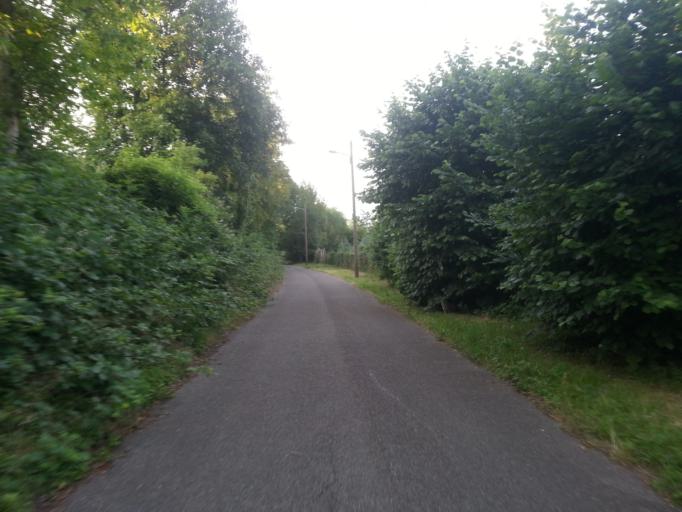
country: DE
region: Baden-Wuerttemberg
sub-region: Karlsruhe Region
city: Mannheim
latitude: 49.4863
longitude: 8.5106
